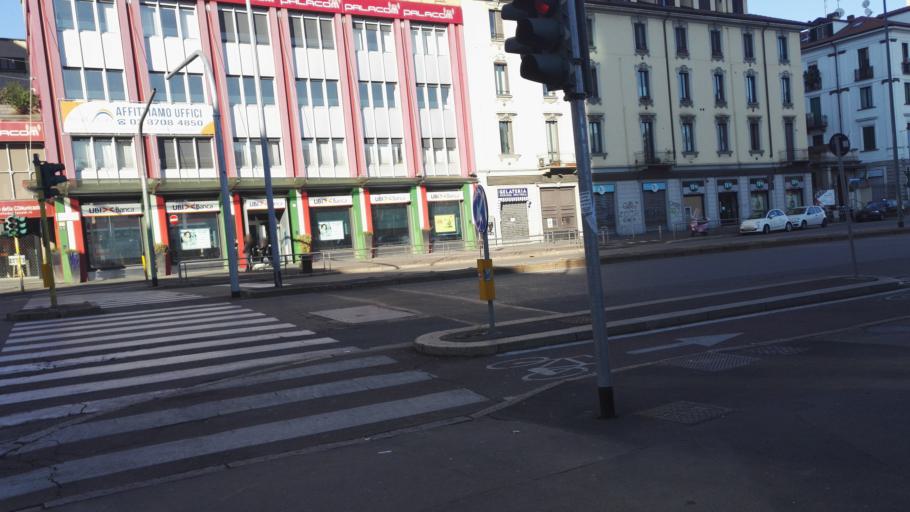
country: IT
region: Lombardy
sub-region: Citta metropolitana di Milano
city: Milano
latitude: 45.4870
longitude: 9.1984
